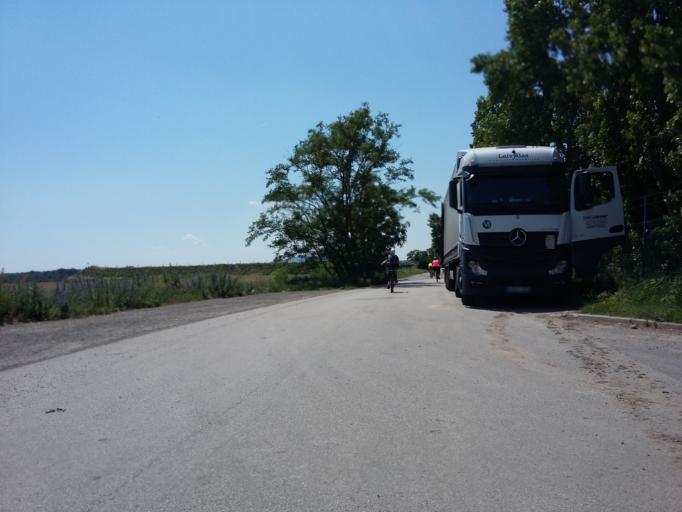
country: AT
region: Lower Austria
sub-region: Politischer Bezirk Ganserndorf
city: Marchegg
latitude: 48.2946
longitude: 16.9682
